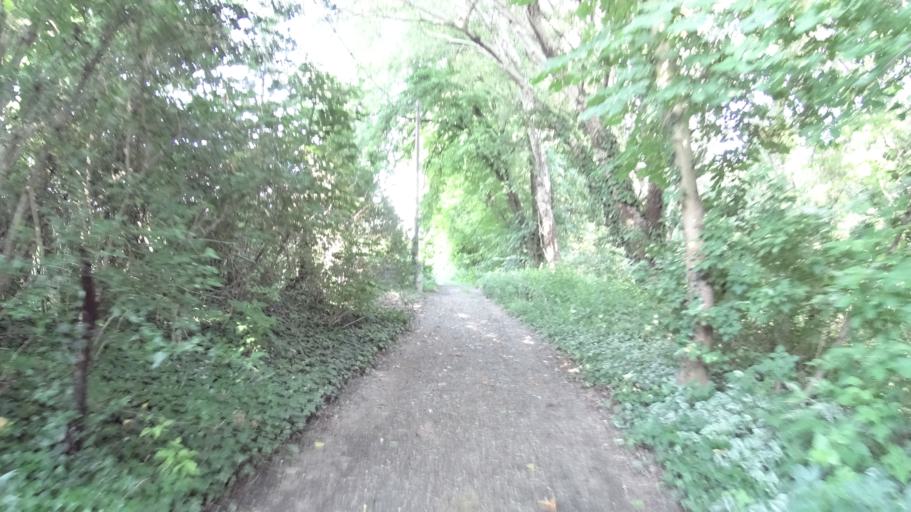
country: HU
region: Pest
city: Kismaros
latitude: 47.8078
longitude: 19.0000
